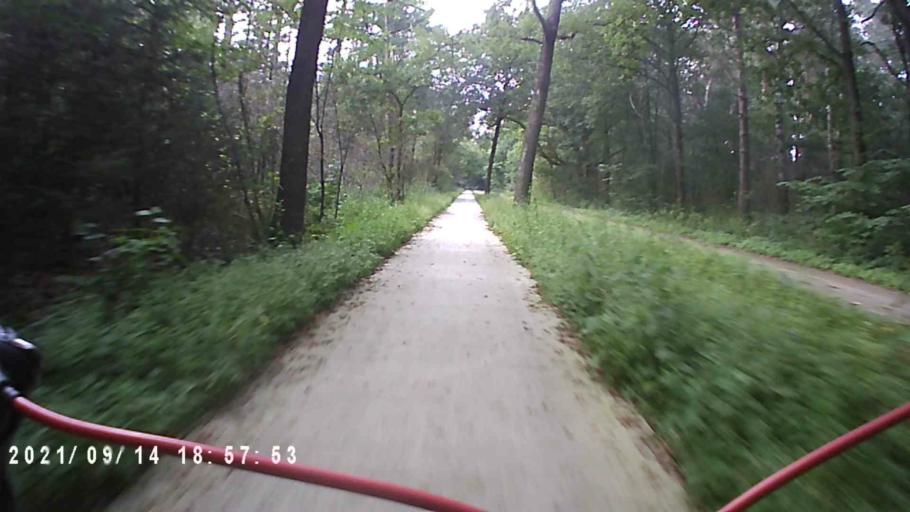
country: NL
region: Drenthe
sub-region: Gemeente Aa en Hunze
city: Anloo
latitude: 53.0301
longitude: 6.7185
